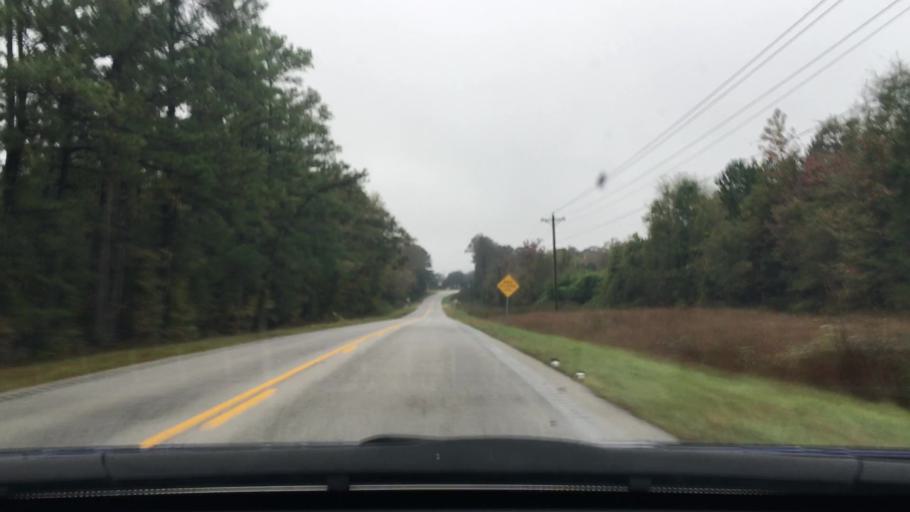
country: US
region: South Carolina
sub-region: Darlington County
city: Darlington
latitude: 34.2474
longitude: -79.9559
